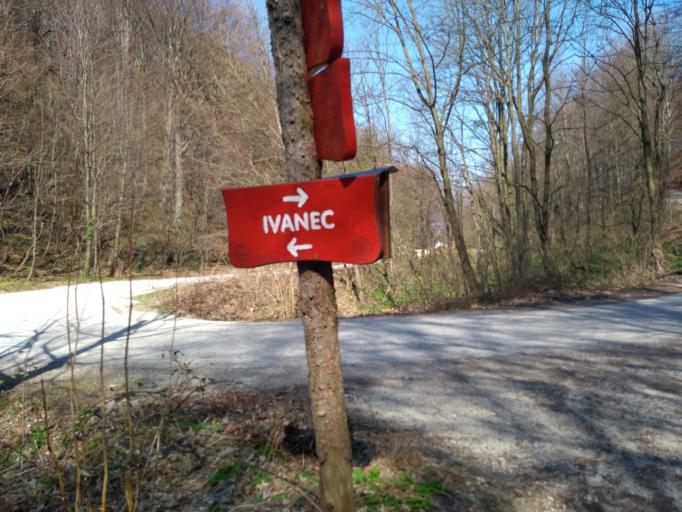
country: HR
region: Varazdinska
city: Ivanec
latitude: 46.1962
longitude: 16.1219
